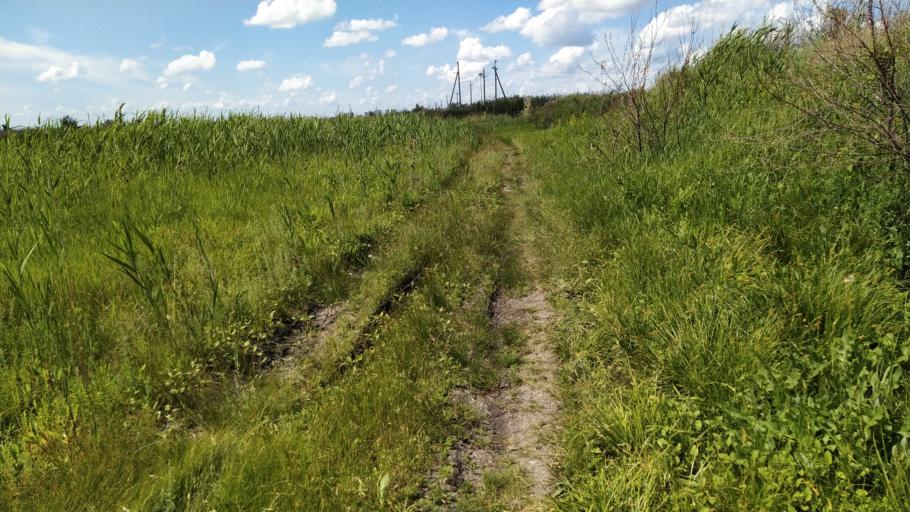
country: RU
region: Rostov
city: Bataysk
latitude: 47.1402
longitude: 39.6692
